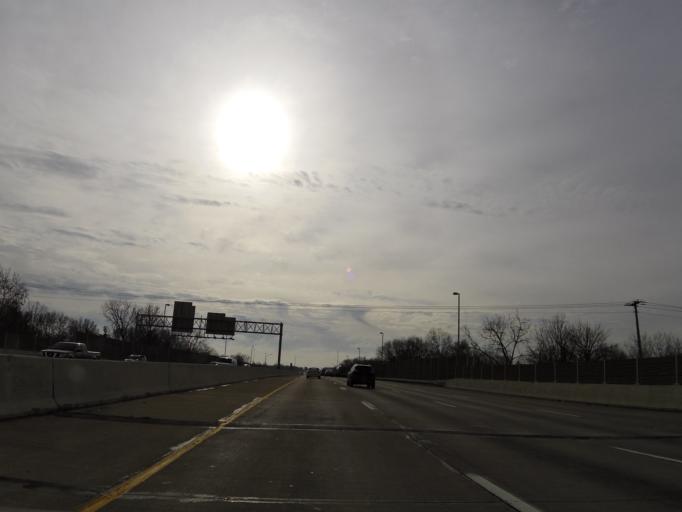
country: US
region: Indiana
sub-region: Marion County
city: Warren Park
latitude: 39.7825
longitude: -86.0318
